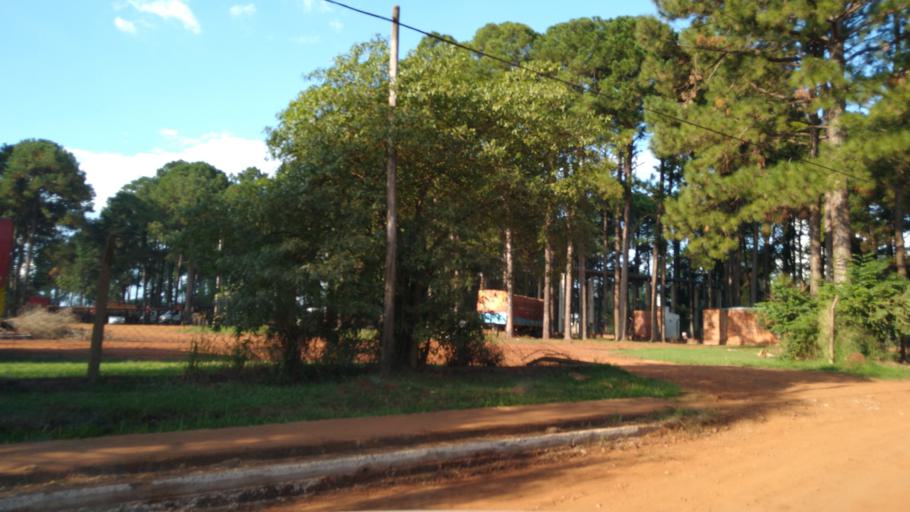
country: AR
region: Misiones
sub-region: Departamento de Capital
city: Posadas
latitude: -27.4047
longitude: -55.9301
